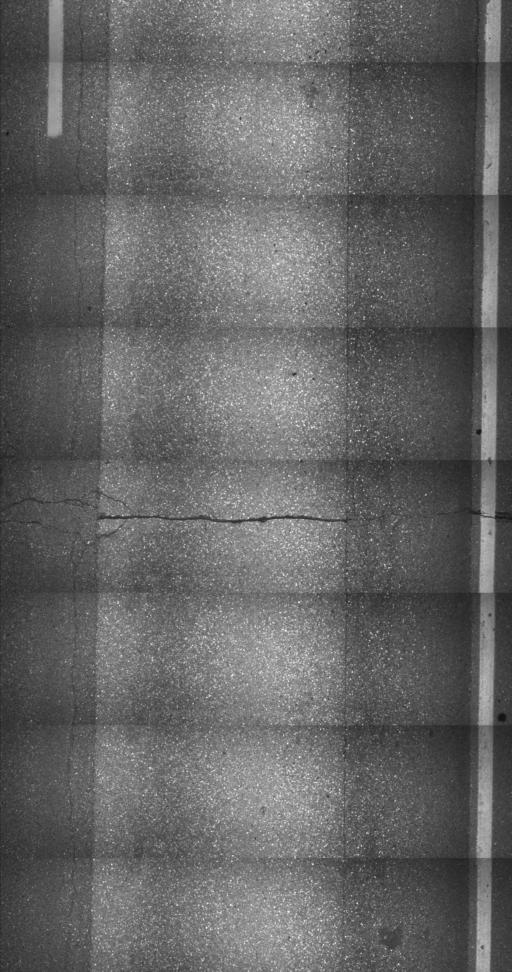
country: US
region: Vermont
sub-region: Chittenden County
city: Williston
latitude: 44.4272
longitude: -73.0251
